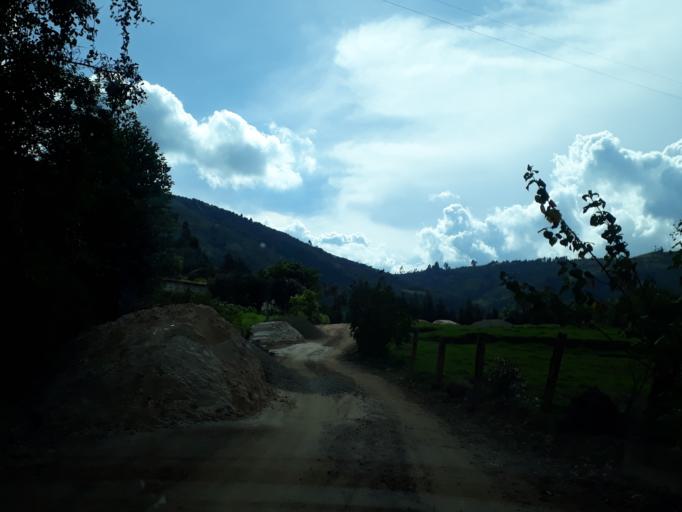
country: CO
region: Boyaca
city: Santa Rosa de Viterbo
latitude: 5.8520
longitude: -72.9614
